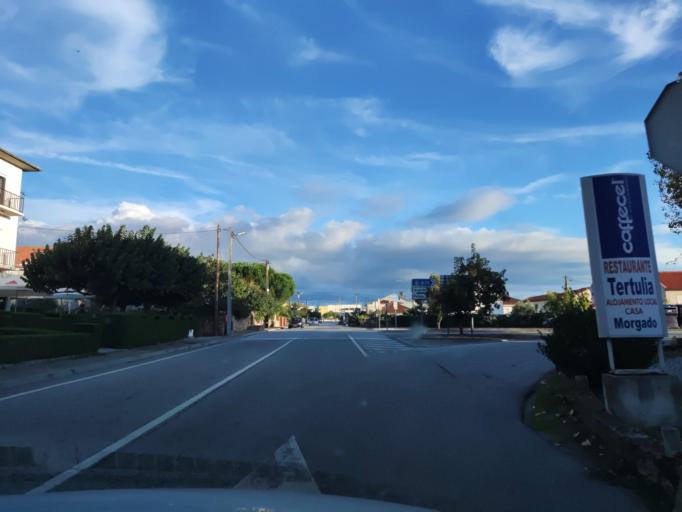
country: ES
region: Castille and Leon
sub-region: Provincia de Salamanca
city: Aldea del Obispo
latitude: 40.7206
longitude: -6.9026
